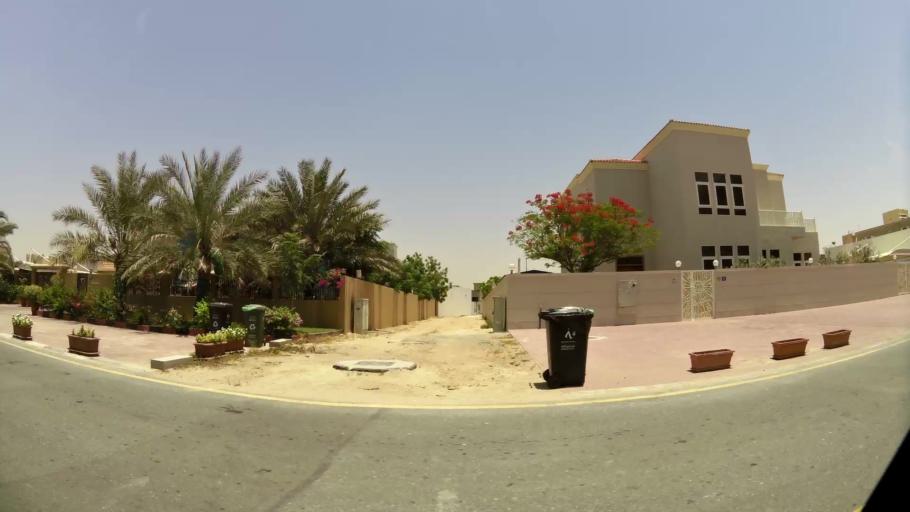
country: AE
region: Dubai
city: Dubai
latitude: 25.0958
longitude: 55.1852
